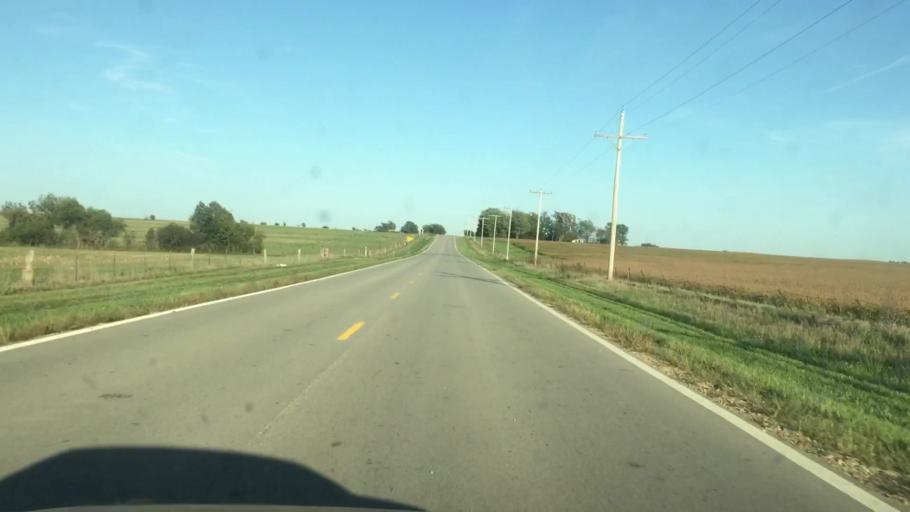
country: US
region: Kansas
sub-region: Brown County
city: Horton
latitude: 39.5876
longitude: -95.5980
